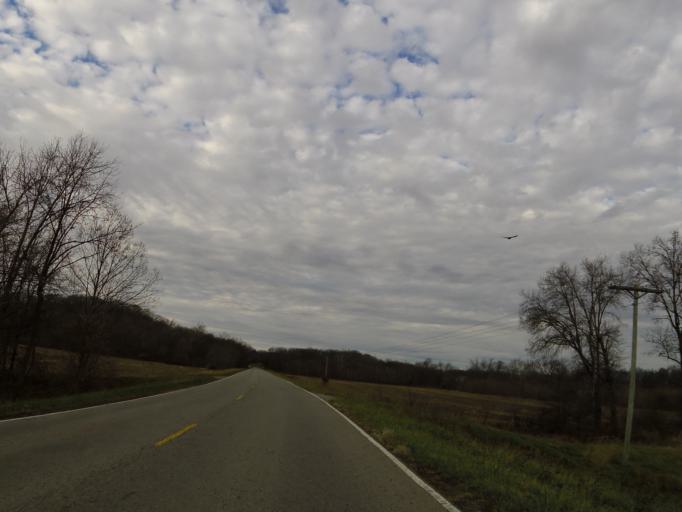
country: US
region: Illinois
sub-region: Jefferson County
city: Mount Vernon
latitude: 38.3792
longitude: -89.0265
